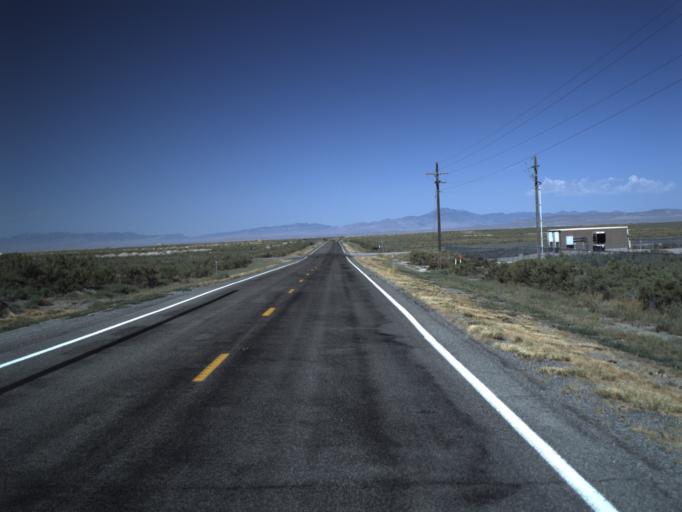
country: US
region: Utah
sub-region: Millard County
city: Delta
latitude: 39.3309
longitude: -112.7064
